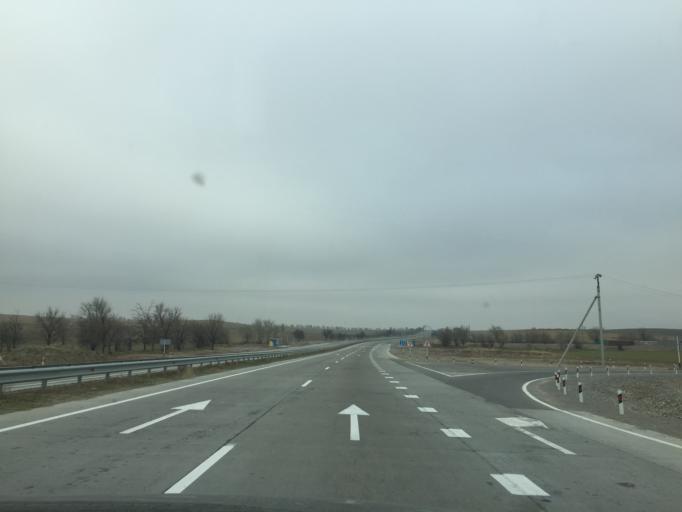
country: KZ
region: Ongtustik Qazaqstan
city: Aksu
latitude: 42.4810
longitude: 69.9170
